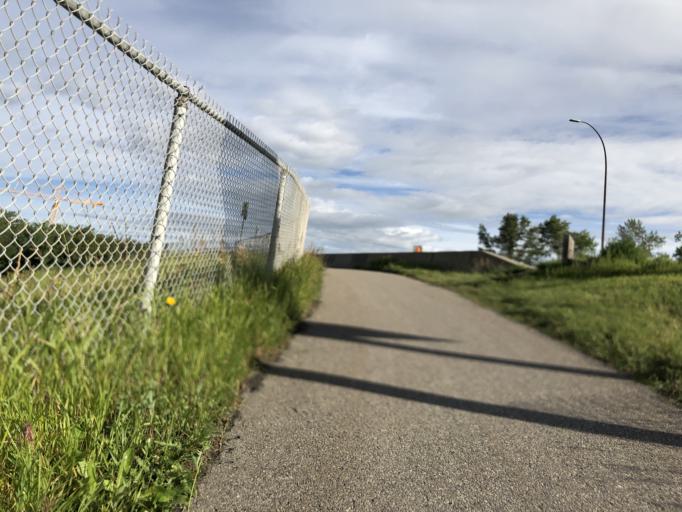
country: CA
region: Alberta
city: Calgary
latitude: 51.0120
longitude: -114.0118
